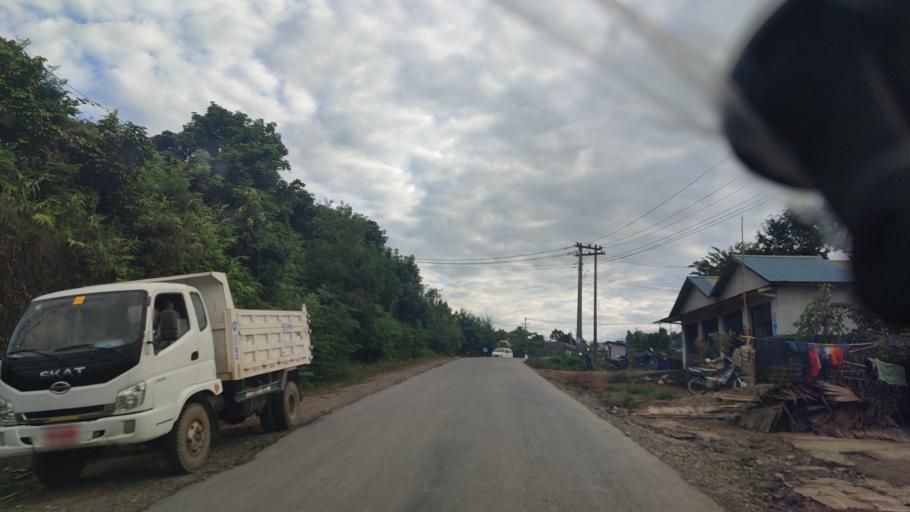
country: MM
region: Magway
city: Minbu
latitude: 19.7647
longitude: 94.0367
